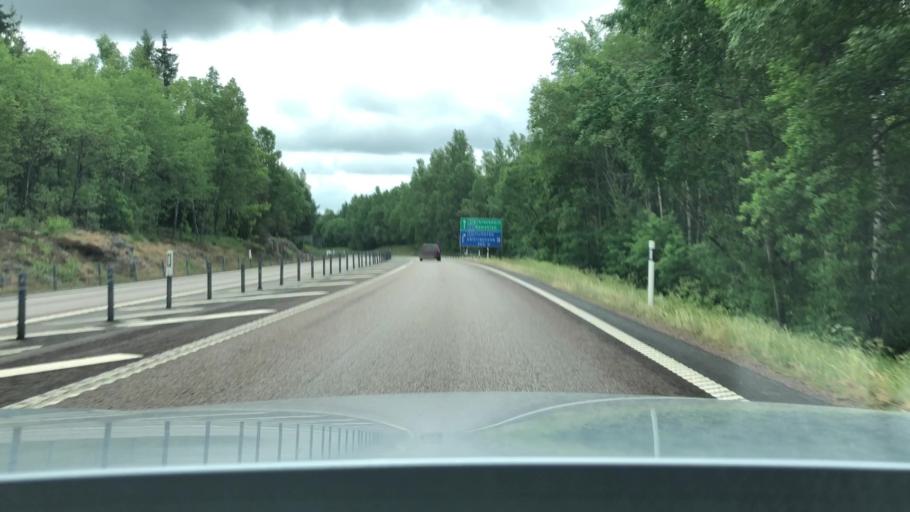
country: SE
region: Vaermland
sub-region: Kristinehamns Kommun
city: Kristinehamn
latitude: 59.3263
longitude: 14.1055
